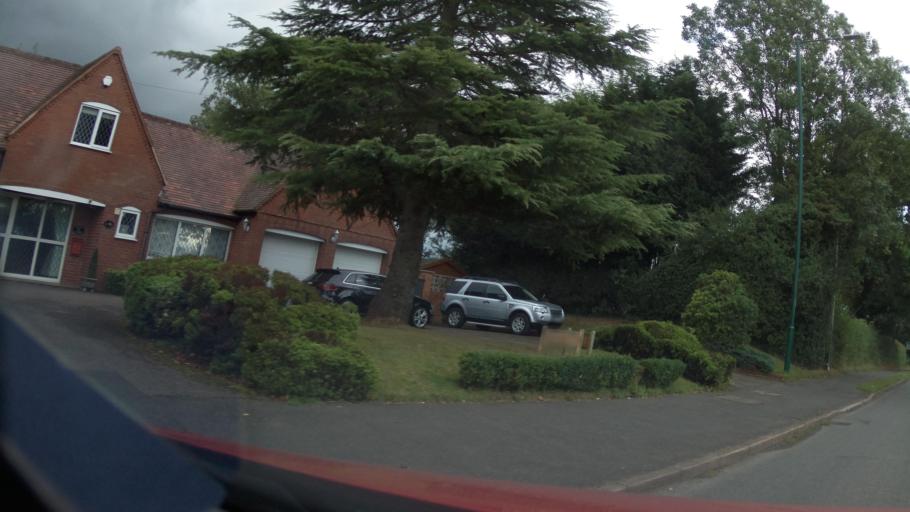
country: GB
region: England
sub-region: Solihull
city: Cheswick Green
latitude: 52.3620
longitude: -1.7805
